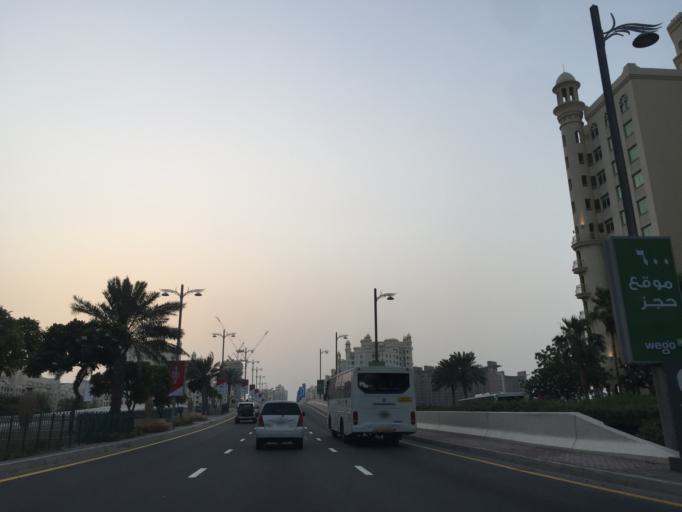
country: AE
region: Dubai
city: Dubai
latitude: 25.1094
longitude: 55.1469
